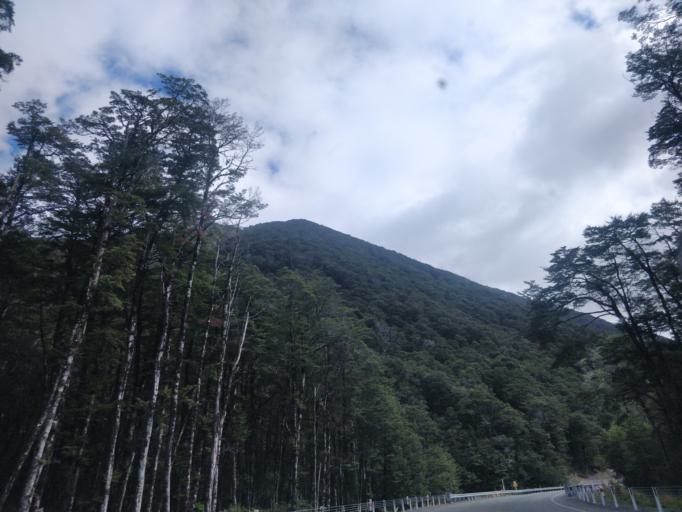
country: NZ
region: West Coast
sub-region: Grey District
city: Greymouth
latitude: -42.9739
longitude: 171.5816
